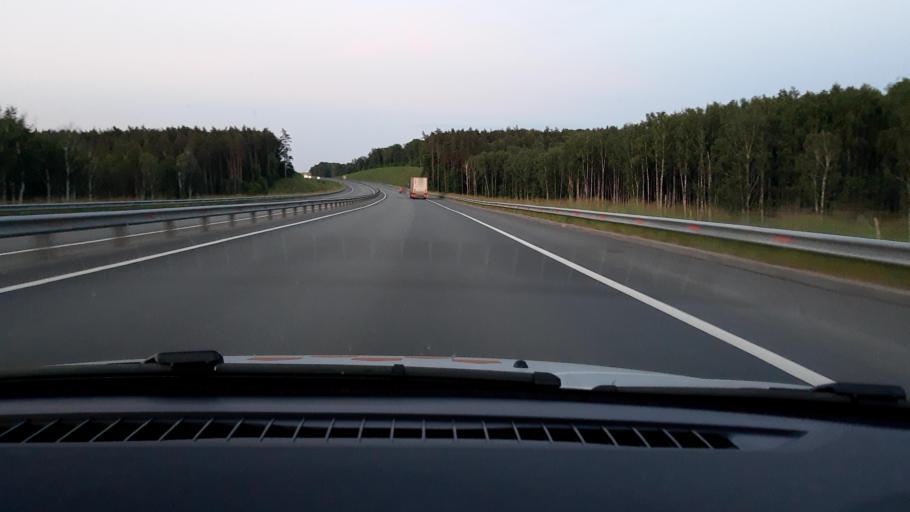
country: RU
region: Nizjnij Novgorod
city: Afonino
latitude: 56.1020
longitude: 44.0171
